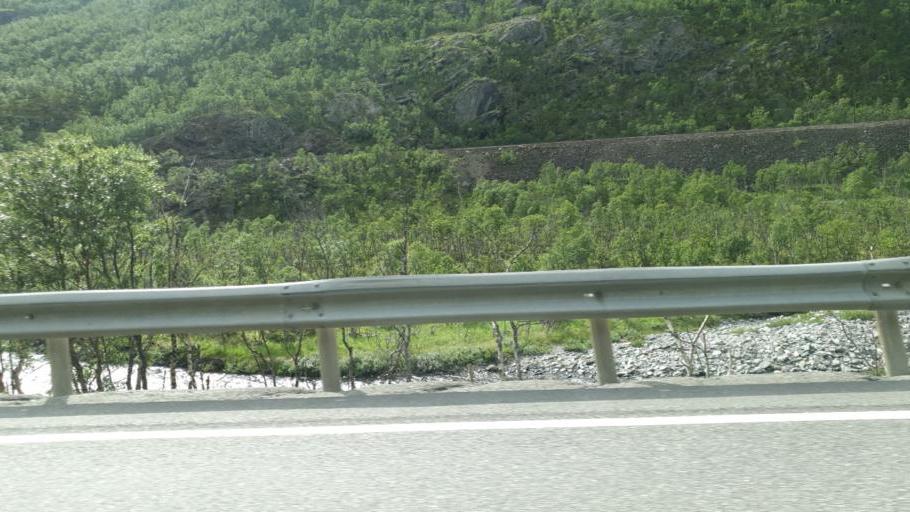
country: NO
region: Sor-Trondelag
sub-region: Oppdal
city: Oppdal
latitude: 62.3268
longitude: 9.6220
